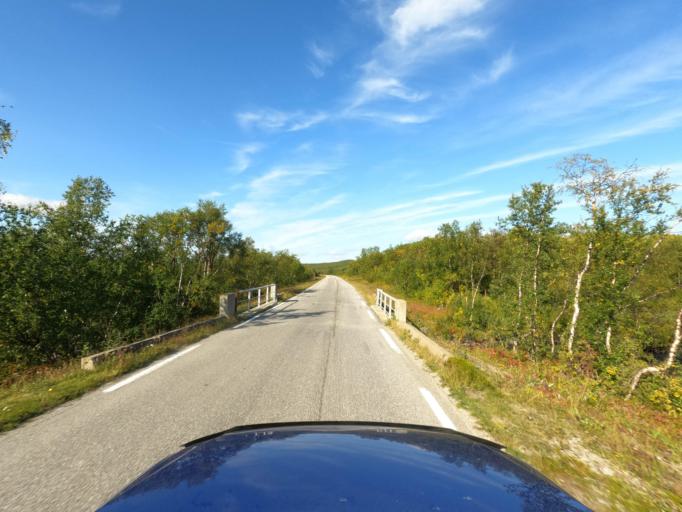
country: NO
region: Finnmark Fylke
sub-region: Porsanger
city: Lakselv
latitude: 69.7561
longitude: 25.2141
